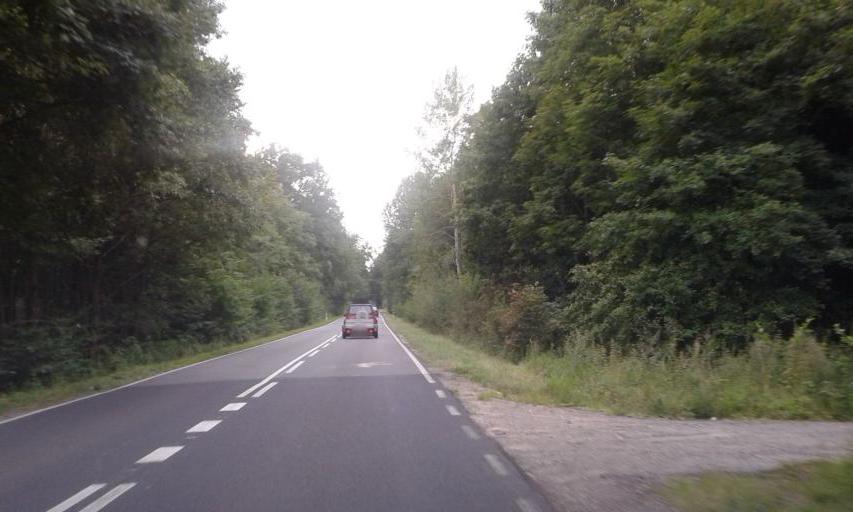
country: PL
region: West Pomeranian Voivodeship
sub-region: Powiat szczecinecki
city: Grzmiaca
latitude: 53.7199
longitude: 16.4981
